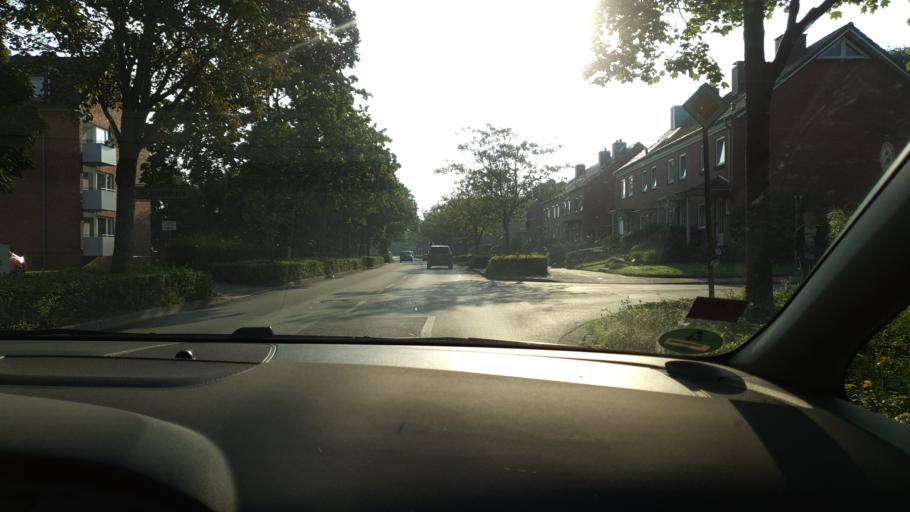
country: DE
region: Schleswig-Holstein
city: Husum
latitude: 54.4852
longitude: 9.0499
